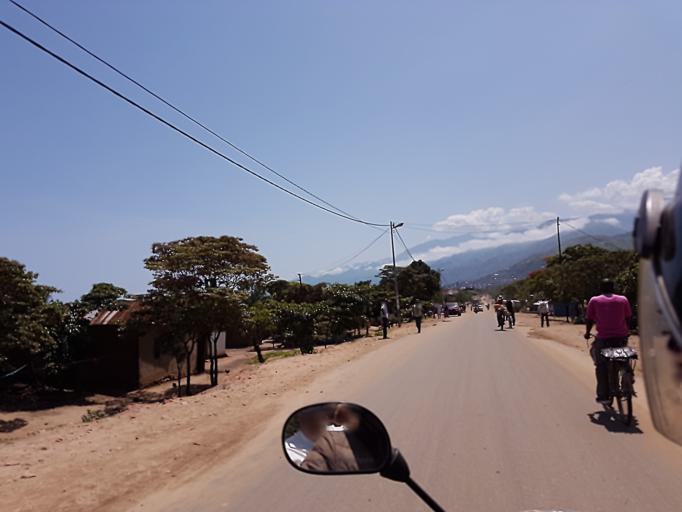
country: CD
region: South Kivu
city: Uvira
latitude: -3.3560
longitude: 29.1539
